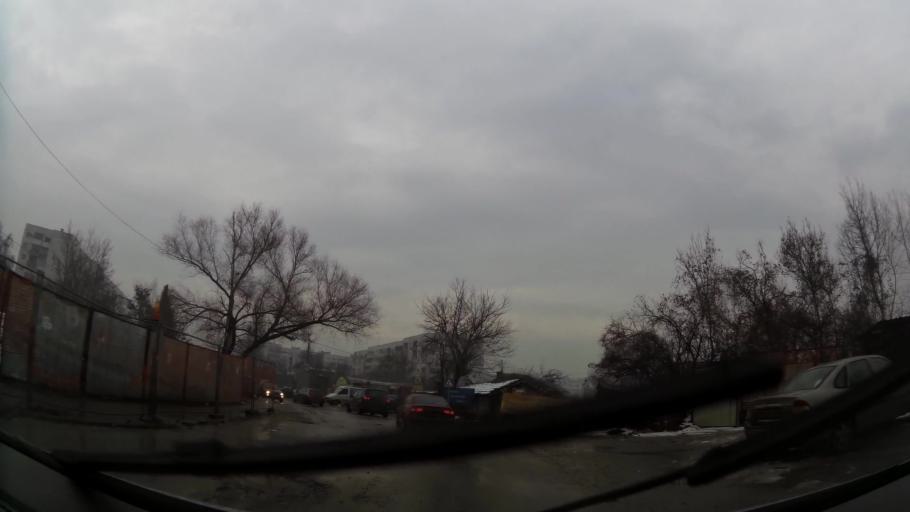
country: BG
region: Sofia-Capital
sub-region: Stolichna Obshtina
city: Sofia
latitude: 42.6843
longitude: 23.2560
